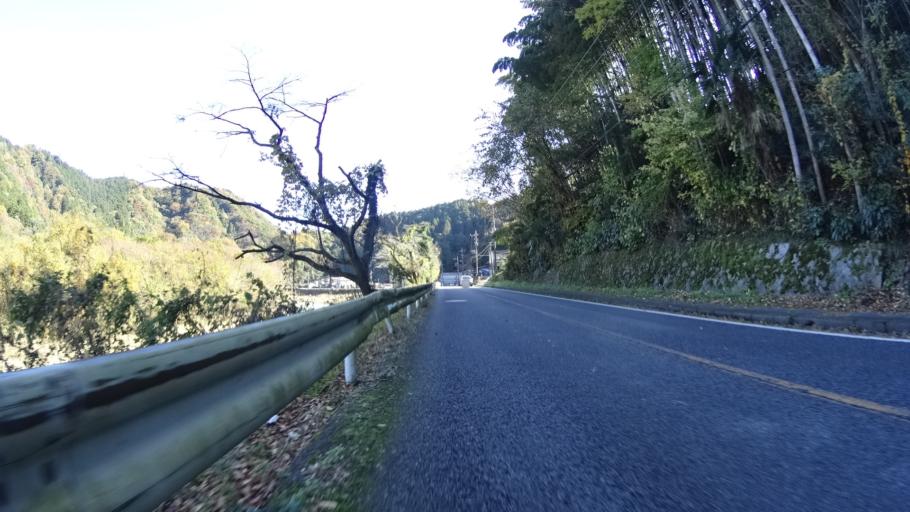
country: JP
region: Kanagawa
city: Zama
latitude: 35.5363
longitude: 139.2786
